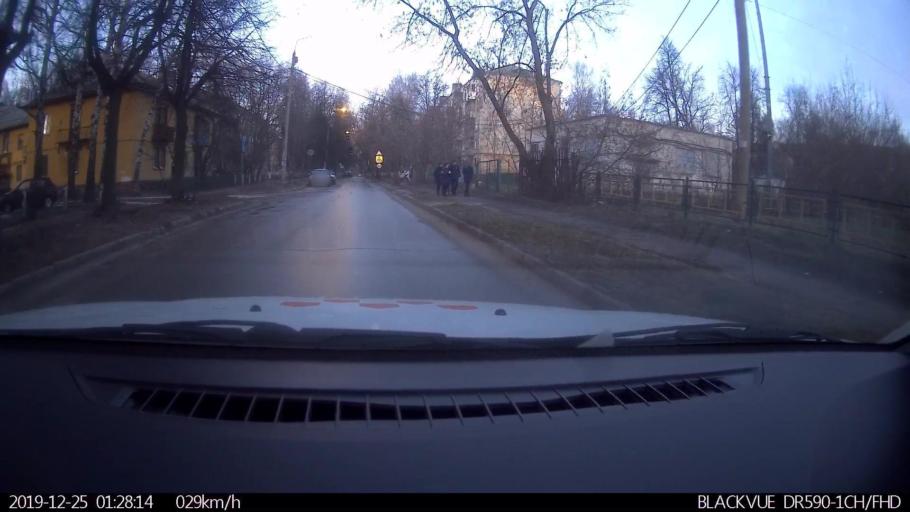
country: RU
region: Nizjnij Novgorod
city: Gorbatovka
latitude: 56.2448
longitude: 43.8380
